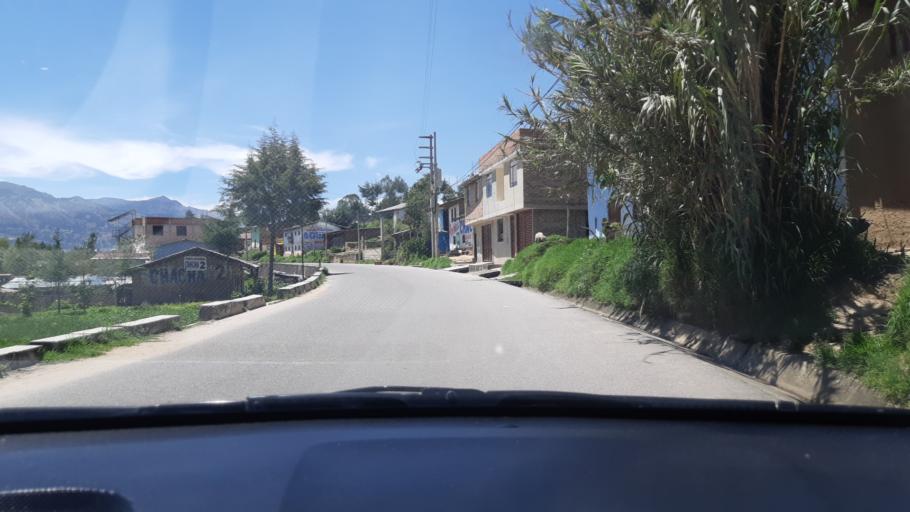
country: PE
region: Cajamarca
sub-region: Provincia de Cajamarca
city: Llacanora
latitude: -7.1819
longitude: -78.4504
